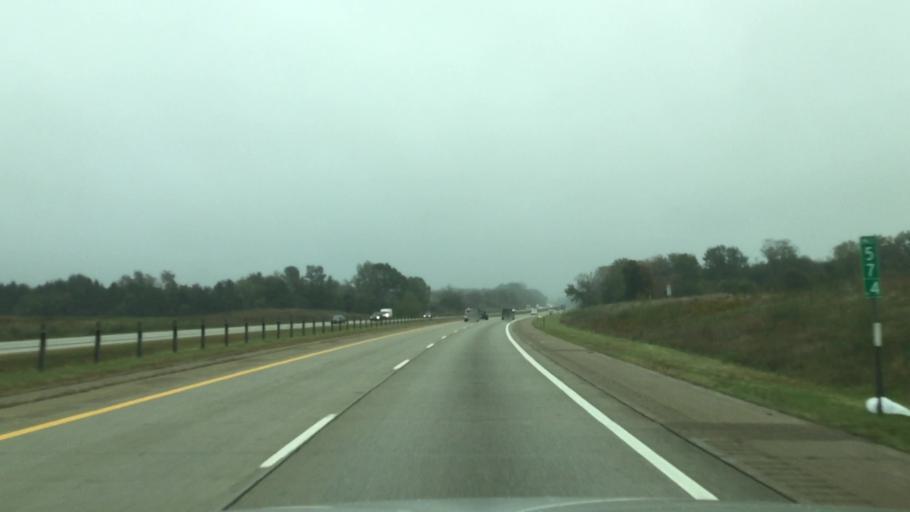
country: US
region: Michigan
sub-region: Van Buren County
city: Paw Paw
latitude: 42.2046
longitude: -85.9458
